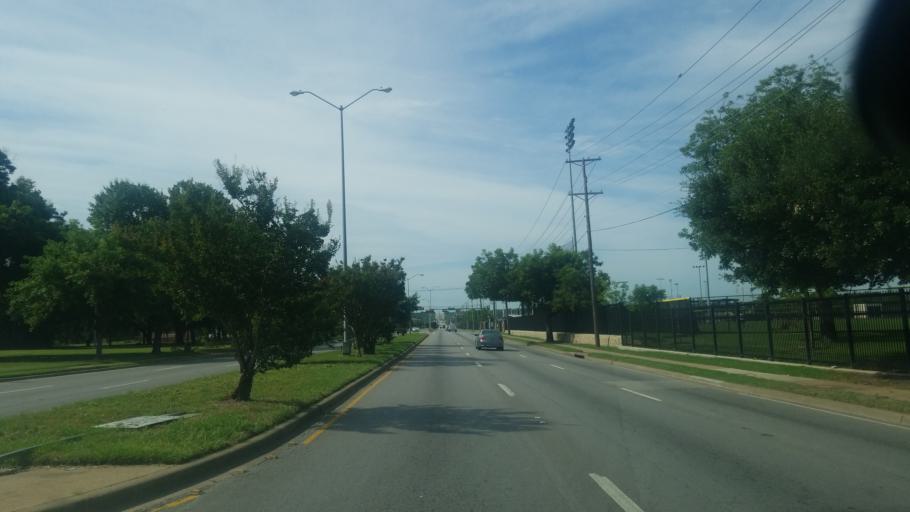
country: US
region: Texas
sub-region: Dallas County
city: Dallas
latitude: 32.7887
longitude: -96.8565
